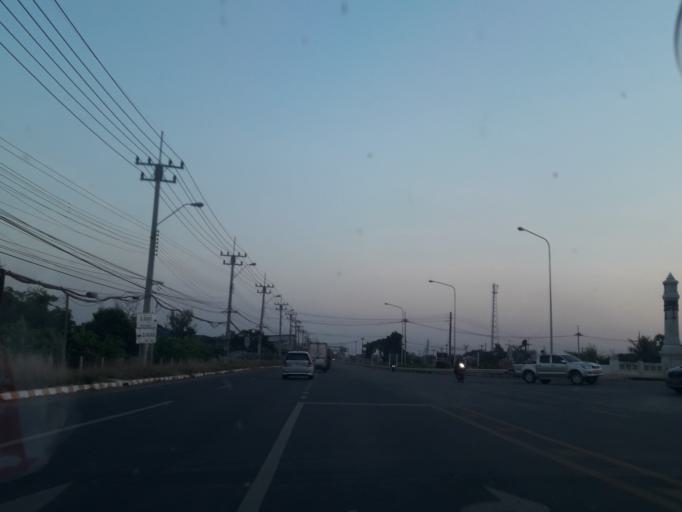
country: TH
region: Pathum Thani
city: Thanyaburi
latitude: 14.0717
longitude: 100.7102
